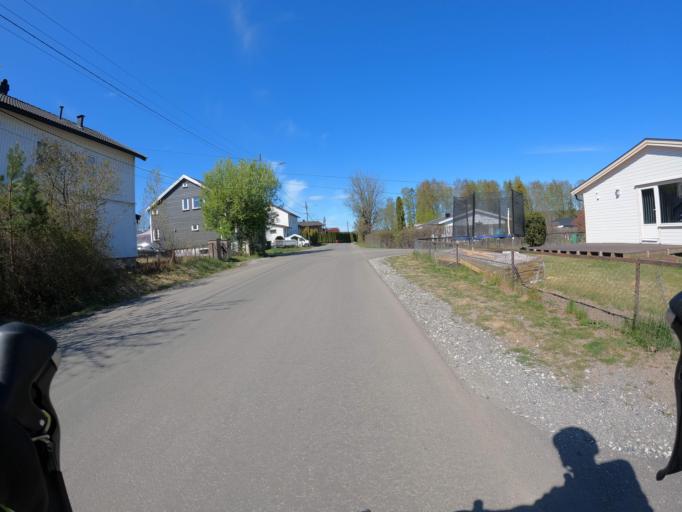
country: NO
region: Akershus
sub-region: Skedsmo
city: Leirsund
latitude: 60.0052
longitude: 11.0432
